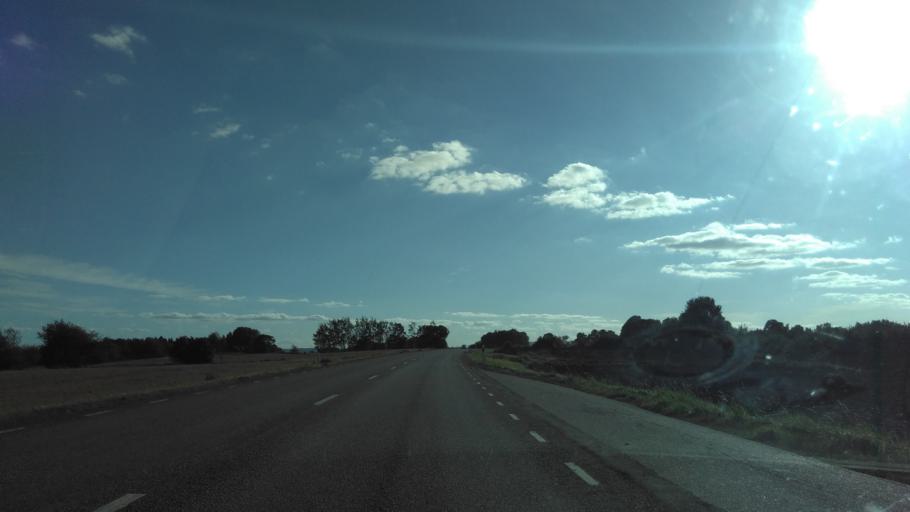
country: SE
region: Vaestra Goetaland
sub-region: Skovde Kommun
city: Skultorp
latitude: 58.2757
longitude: 13.7523
